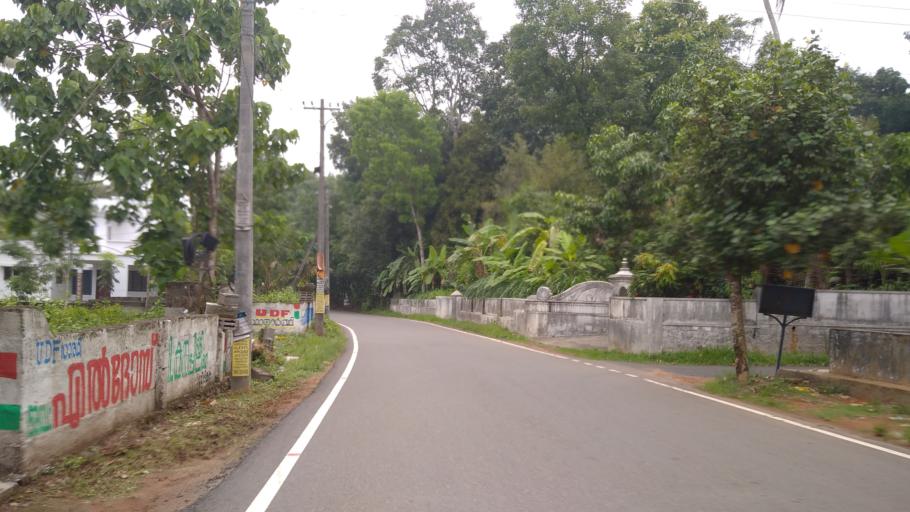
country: IN
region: Kerala
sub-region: Ernakulam
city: Perumpavur
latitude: 10.1232
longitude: 76.5399
